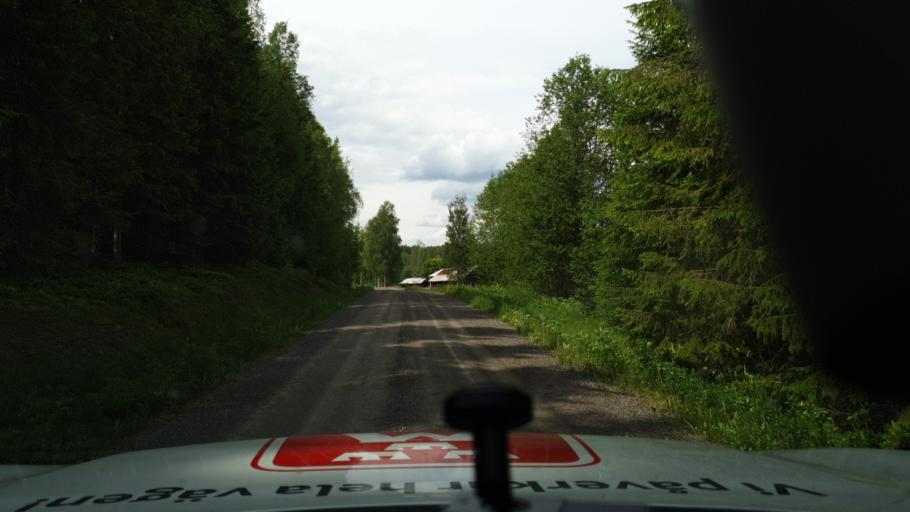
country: SE
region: Vaermland
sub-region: Torsby Kommun
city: Torsby
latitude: 59.9802
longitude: 12.8407
